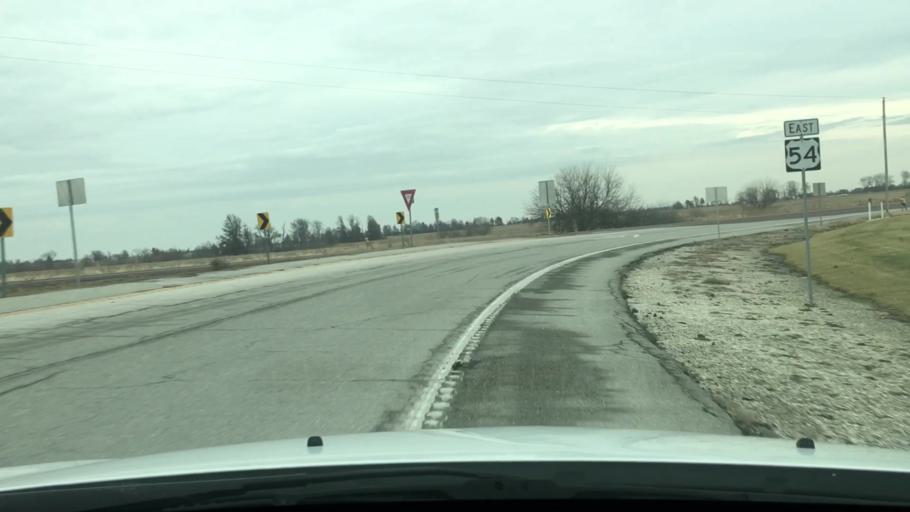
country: US
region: Missouri
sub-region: Audrain County
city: Vandalia
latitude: 39.2807
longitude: -91.6437
